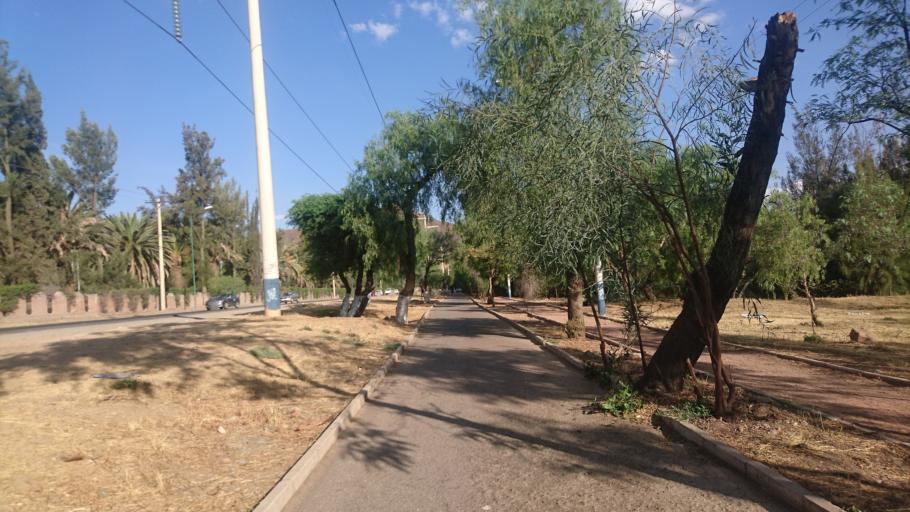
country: BO
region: Cochabamba
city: Cochabamba
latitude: -17.4030
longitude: -66.1319
